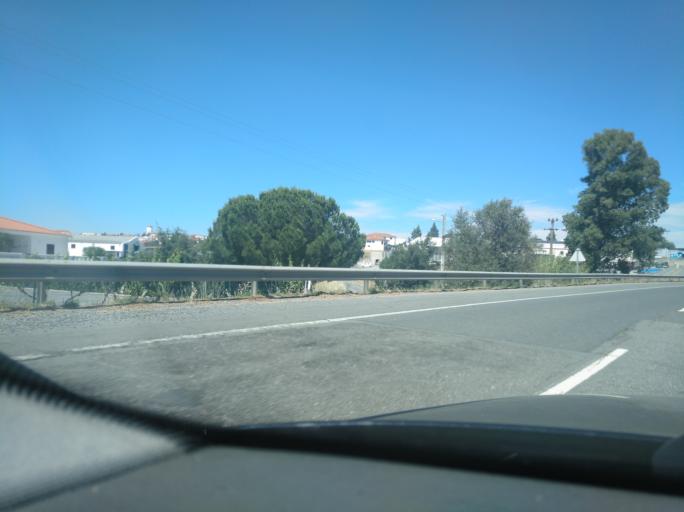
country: PT
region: Beja
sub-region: Castro Verde
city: Castro Verde
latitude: 37.6940
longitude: -8.0932
